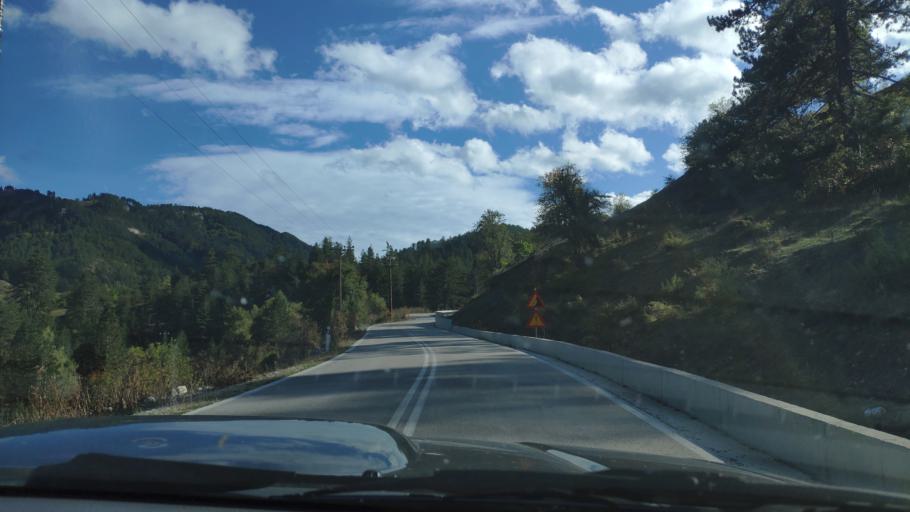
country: AL
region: Korce
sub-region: Rrethi i Devollit
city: Miras
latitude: 40.4011
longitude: 20.8823
